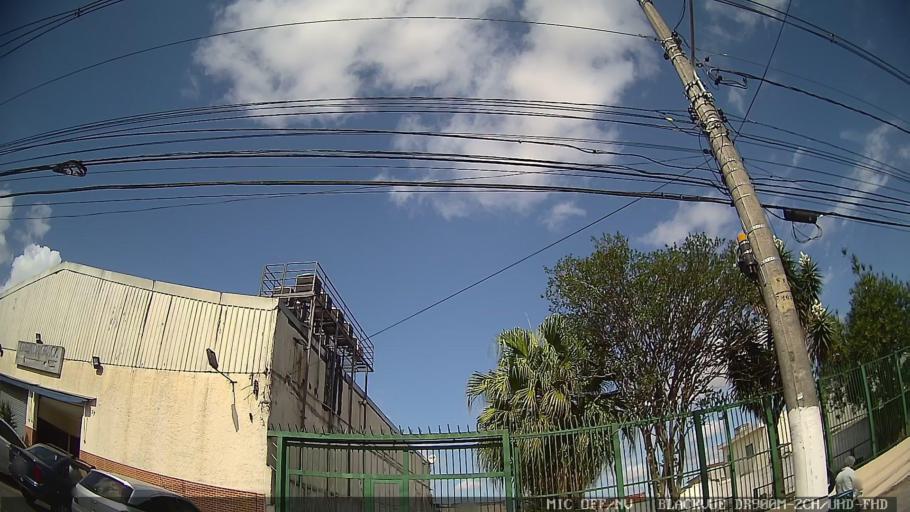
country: BR
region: Sao Paulo
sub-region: Guarulhos
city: Guarulhos
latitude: -23.4997
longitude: -46.4676
